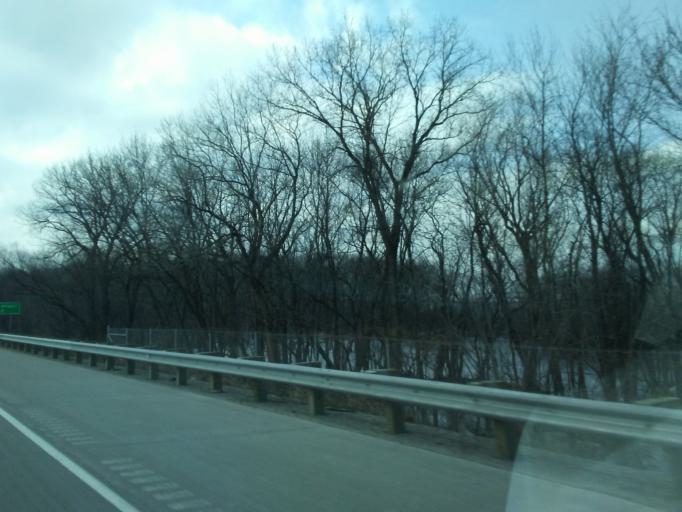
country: US
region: Wisconsin
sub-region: La Crosse County
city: French Island
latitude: 43.8628
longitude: -91.2479
